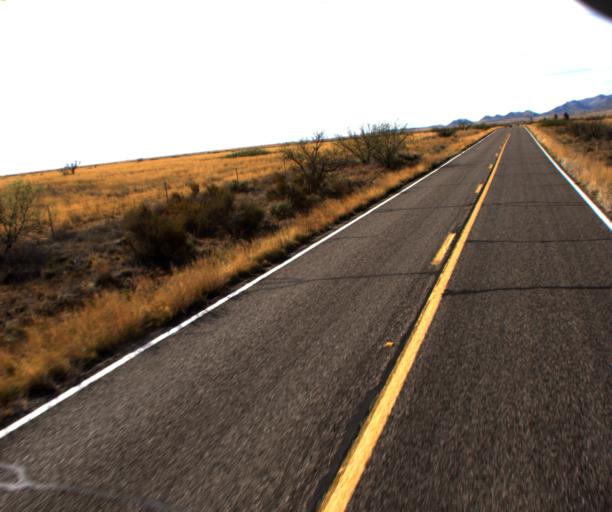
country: US
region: Arizona
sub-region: Cochise County
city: Willcox
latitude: 32.0894
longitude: -109.5300
